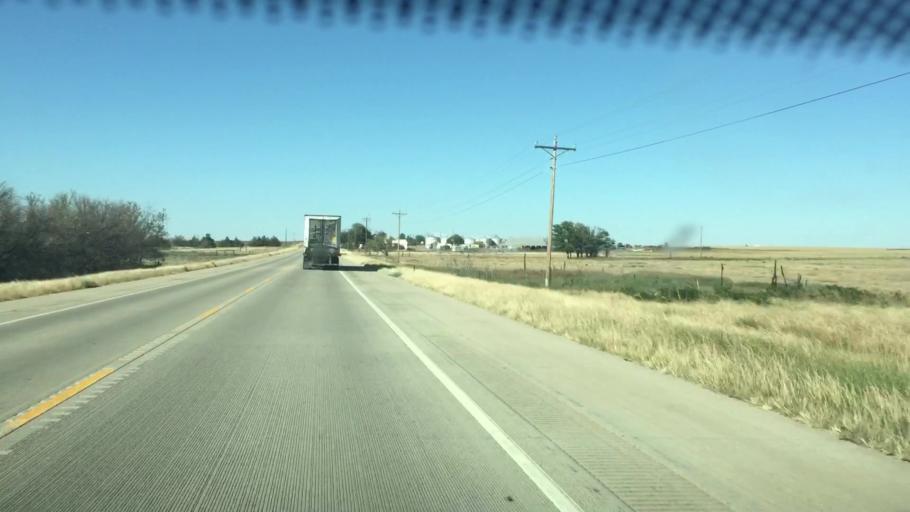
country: US
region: Colorado
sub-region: Kiowa County
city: Eads
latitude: 38.4599
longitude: -102.7307
